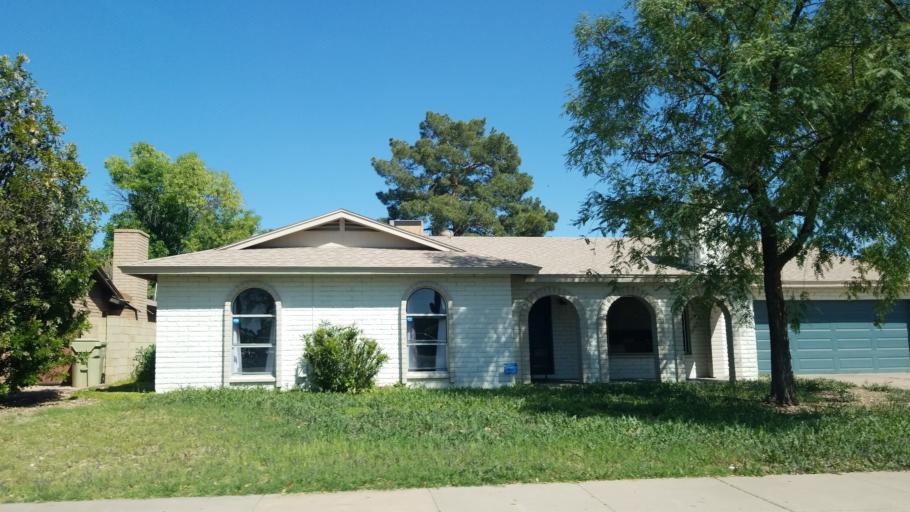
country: US
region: Arizona
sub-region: Maricopa County
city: Glendale
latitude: 33.5599
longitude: -112.1732
